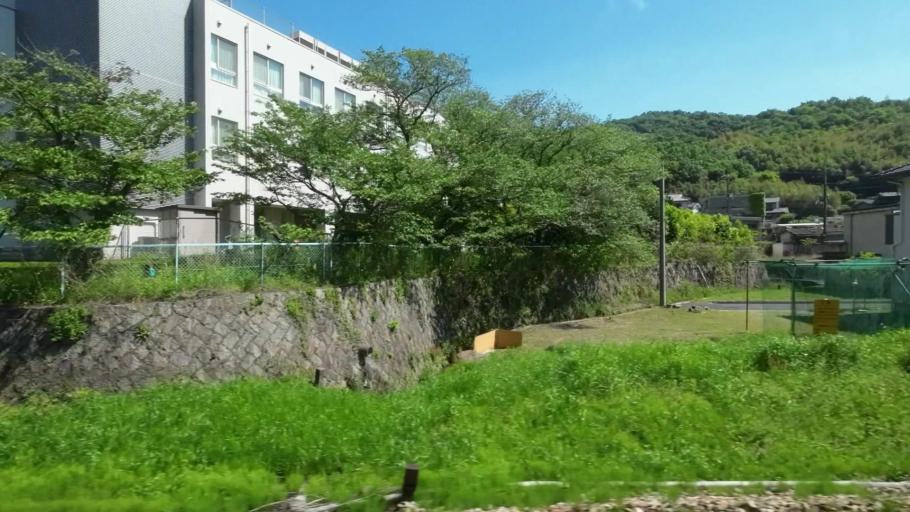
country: JP
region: Hiroshima
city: Fukuyama
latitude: 34.4621
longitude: 133.2860
